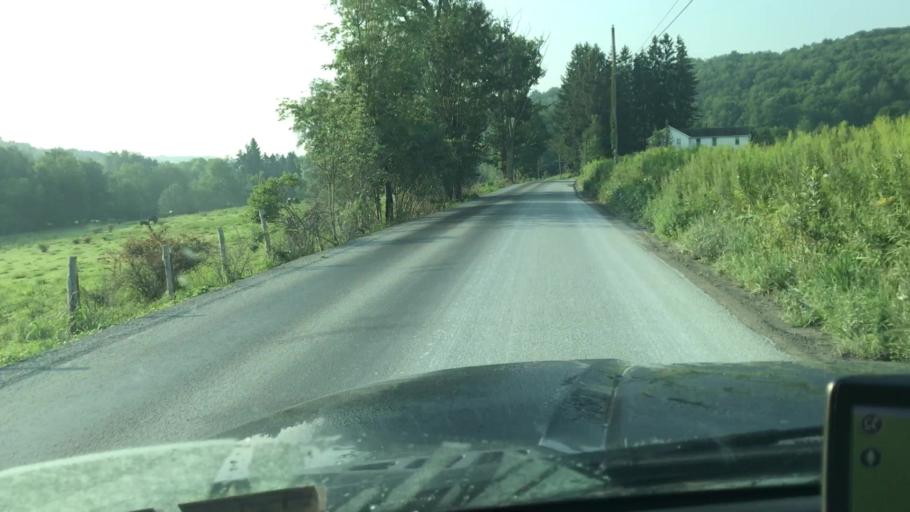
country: US
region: Pennsylvania
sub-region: Wyoming County
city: Factoryville
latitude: 41.6674
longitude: -75.8101
